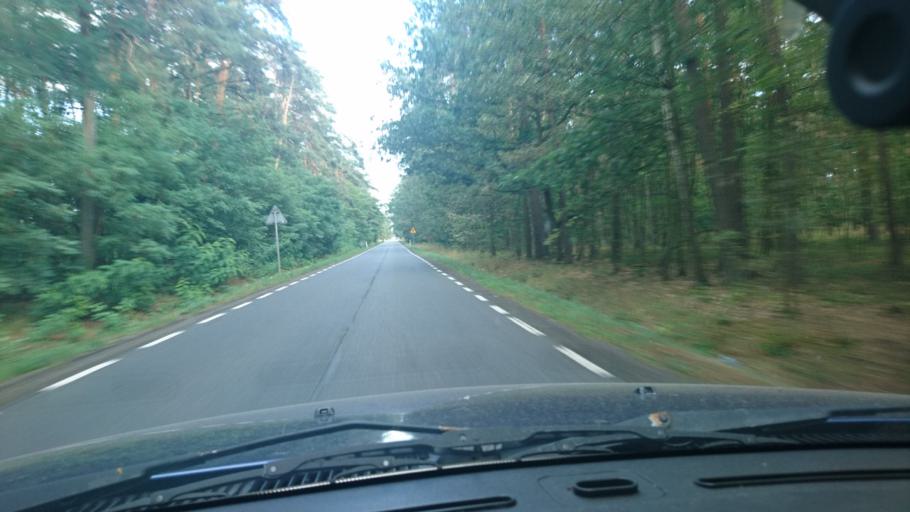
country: PL
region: Greater Poland Voivodeship
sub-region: Powiat ostrzeszowski
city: Ostrzeszow
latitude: 51.4363
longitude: 17.8828
